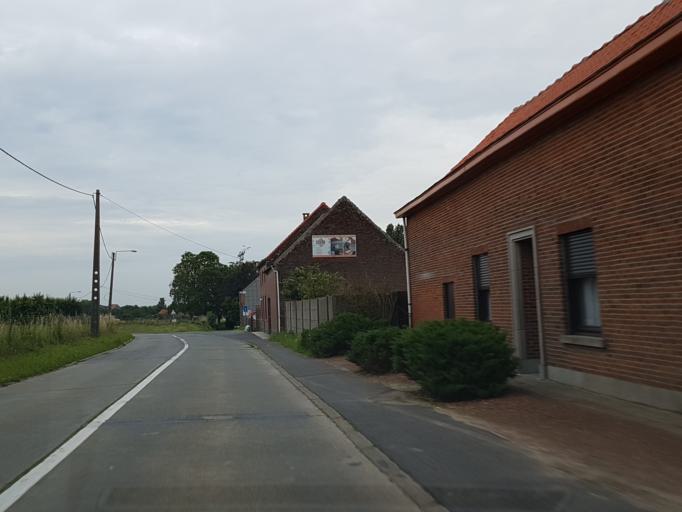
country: BE
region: Flanders
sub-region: Provincie Vlaams-Brabant
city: Wemmel
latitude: 50.9316
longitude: 4.2708
